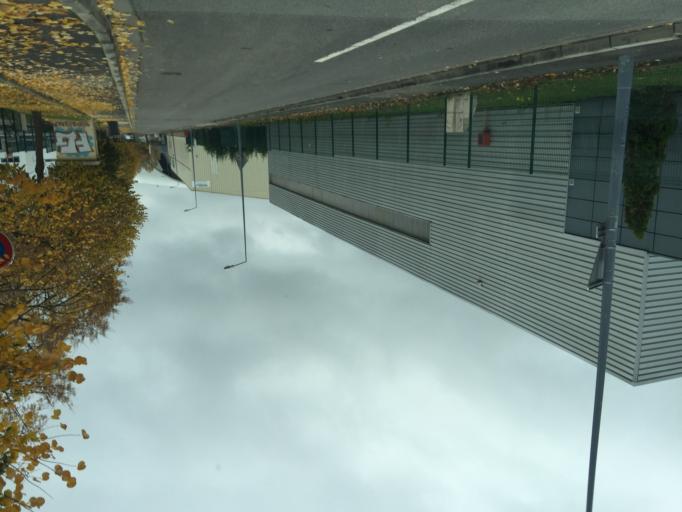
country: FR
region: Rhone-Alpes
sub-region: Departement de la Loire
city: Saint-Etienne
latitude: 45.4522
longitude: 4.3963
